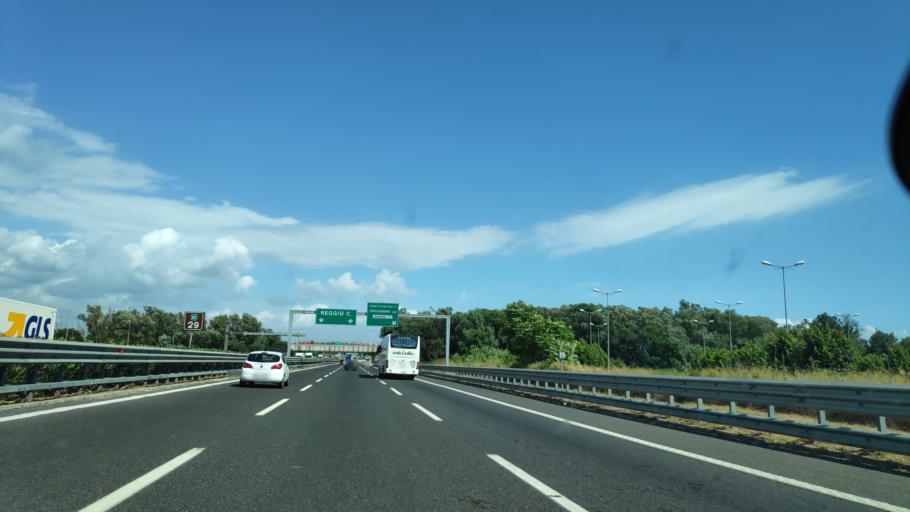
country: IT
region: Campania
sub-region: Provincia di Salerno
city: Pagliarone
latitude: 40.6361
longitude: 14.9110
